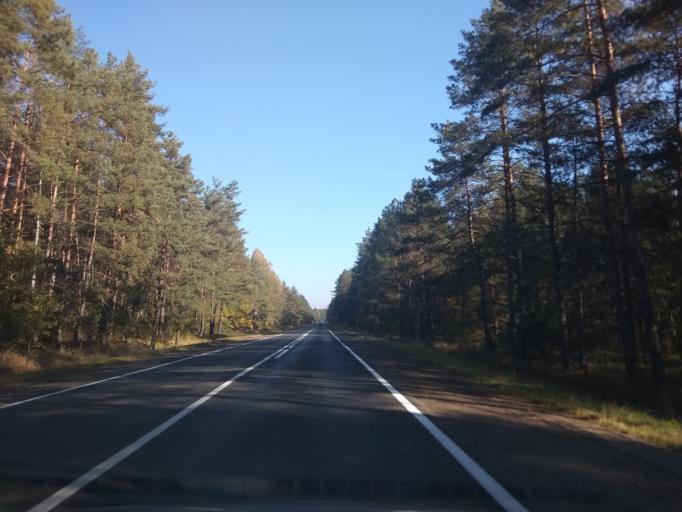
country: BY
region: Brest
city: Baranovichi
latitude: 53.0416
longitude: 25.8150
